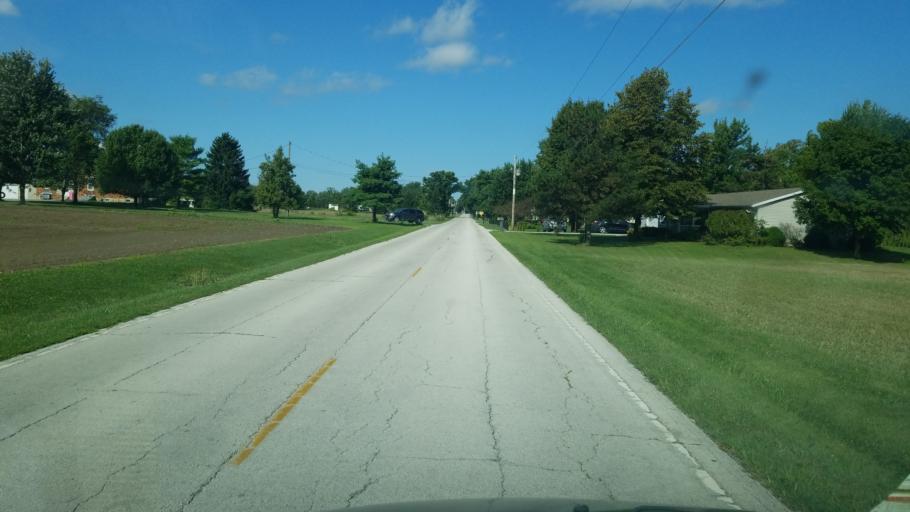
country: US
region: Ohio
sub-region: Seneca County
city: Fostoria
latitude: 41.1083
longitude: -83.5028
